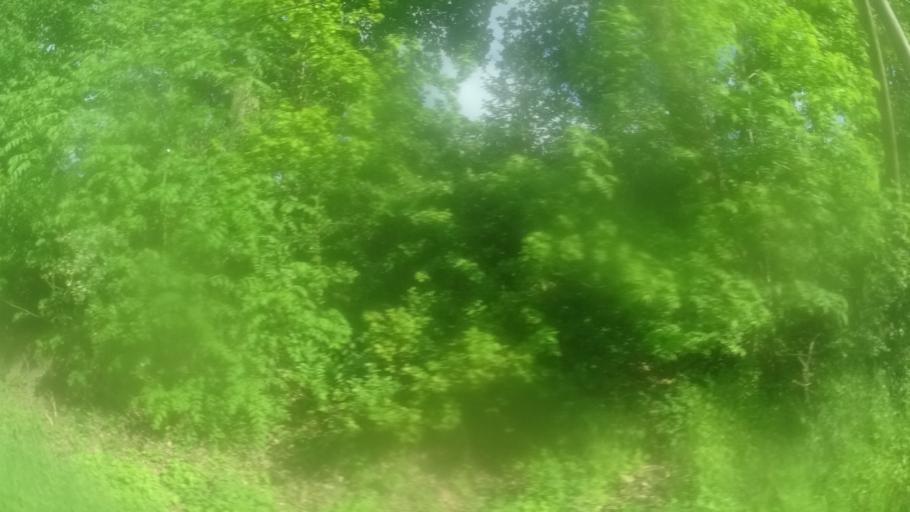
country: DE
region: Thuringia
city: Rudolstadt
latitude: 50.7010
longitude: 11.3569
